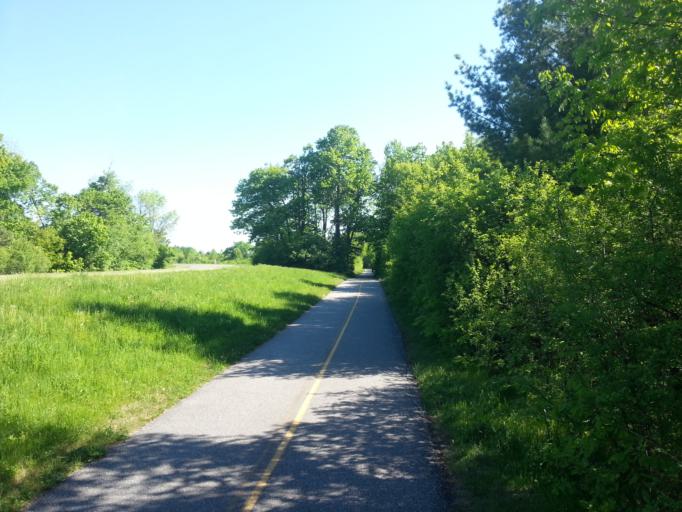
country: CA
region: Quebec
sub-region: Outaouais
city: Gatineau
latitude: 45.4419
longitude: -75.7607
